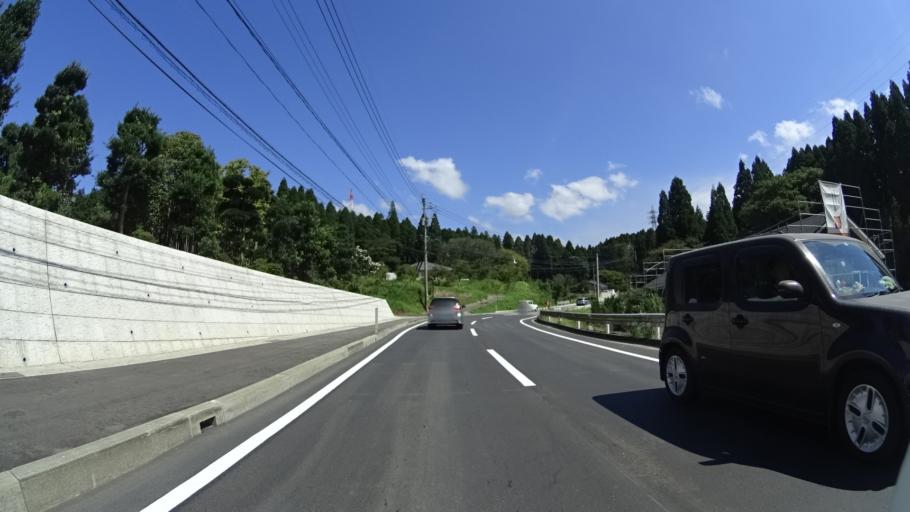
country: JP
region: Kumamoto
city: Aso
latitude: 32.8843
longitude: 130.9964
